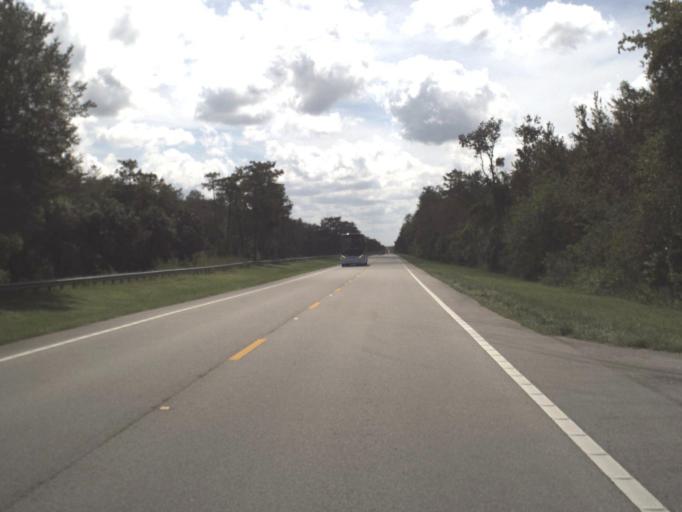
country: US
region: Florida
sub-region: Collier County
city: Immokalee
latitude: 26.2413
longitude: -81.3427
